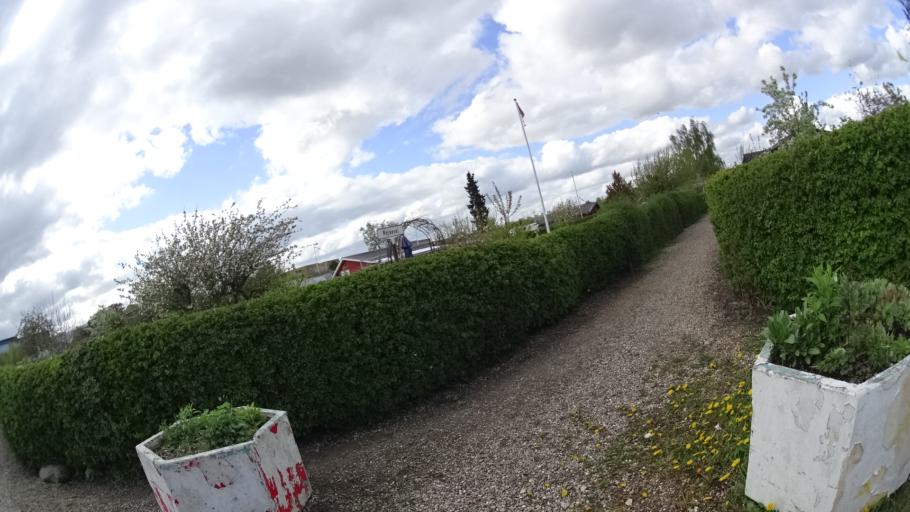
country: DK
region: Central Jutland
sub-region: Arhus Kommune
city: Stavtrup
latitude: 56.1333
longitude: 10.1613
